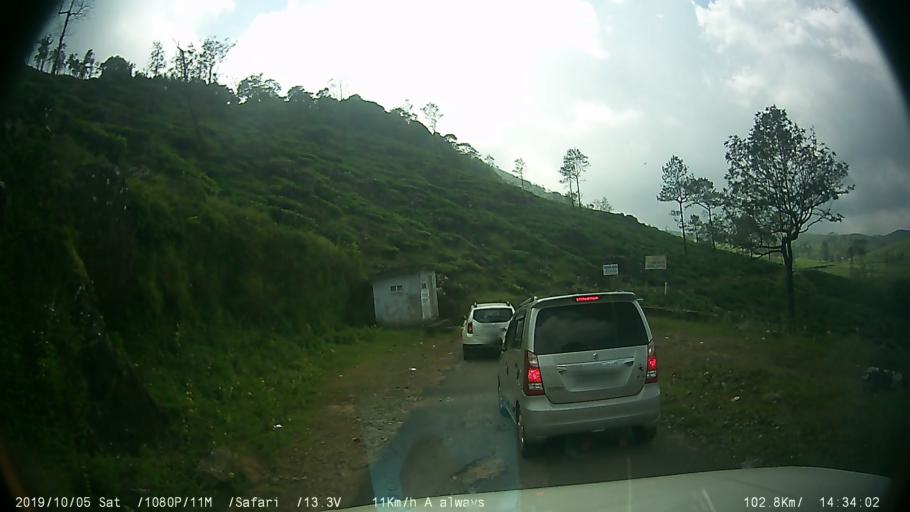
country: IN
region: Kerala
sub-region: Kottayam
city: Erattupetta
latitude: 9.6157
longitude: 76.9655
